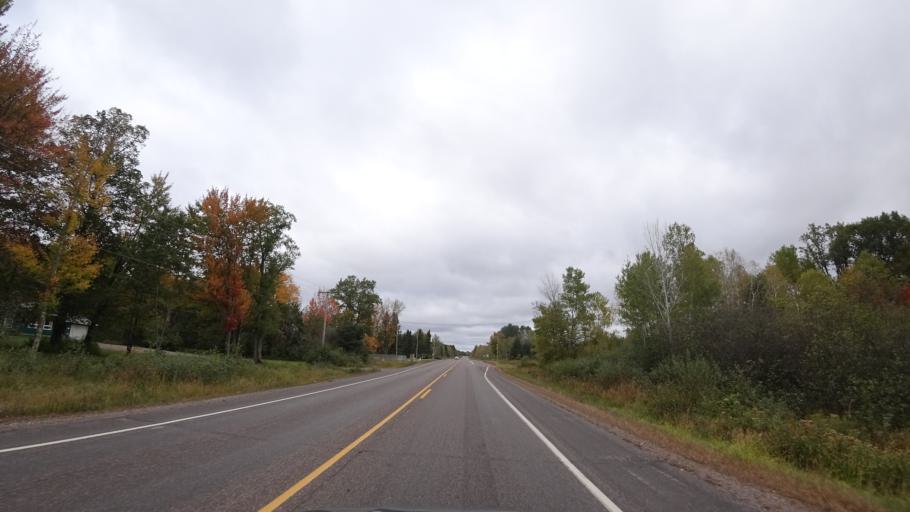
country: US
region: Wisconsin
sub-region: Rusk County
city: Ladysmith
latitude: 45.4349
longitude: -91.1109
